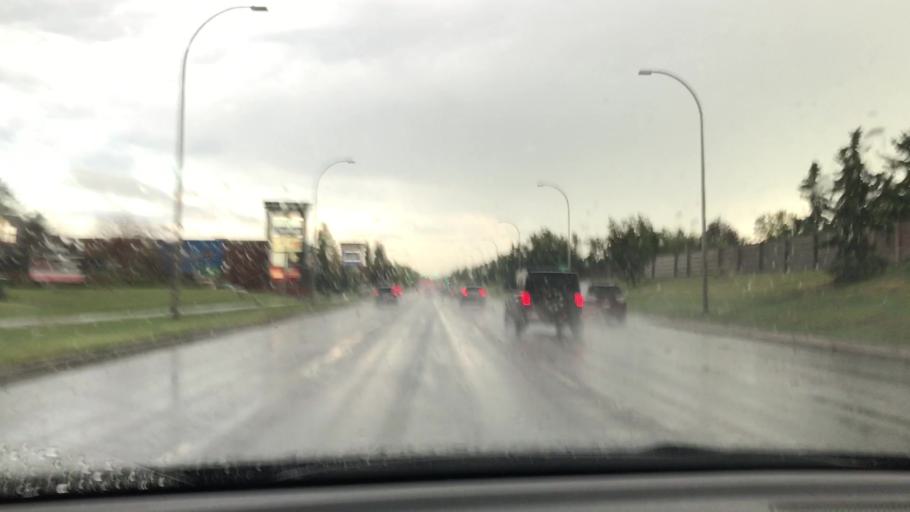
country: CA
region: Alberta
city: Edmonton
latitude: 53.4768
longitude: -113.4956
